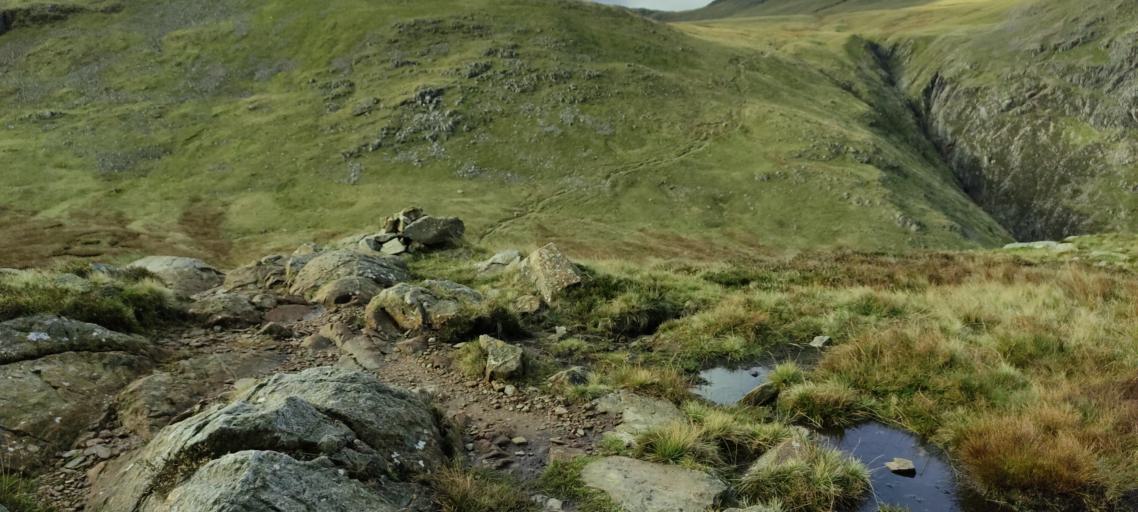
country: GB
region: England
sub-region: Cumbria
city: Ambleside
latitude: 54.4263
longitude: -3.1281
